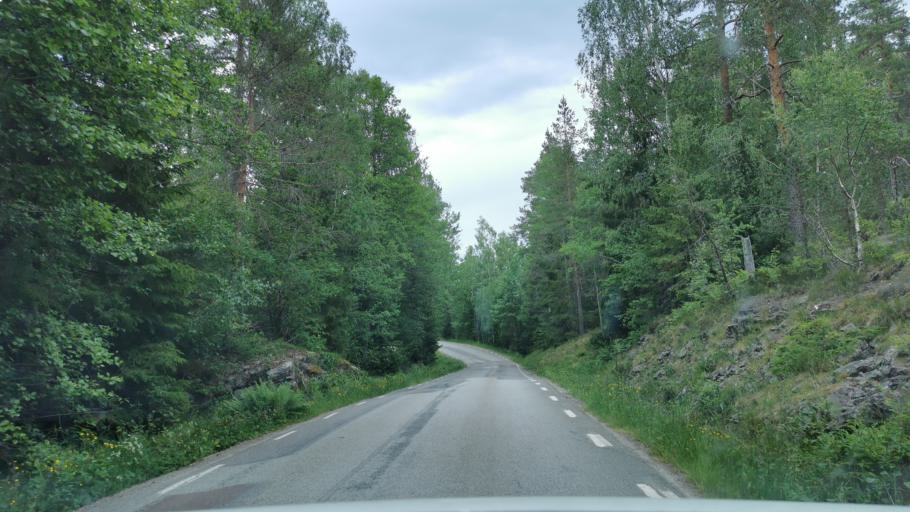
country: SE
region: Vaestra Goetaland
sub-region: Bengtsfors Kommun
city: Dals Langed
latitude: 58.8648
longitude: 12.4026
